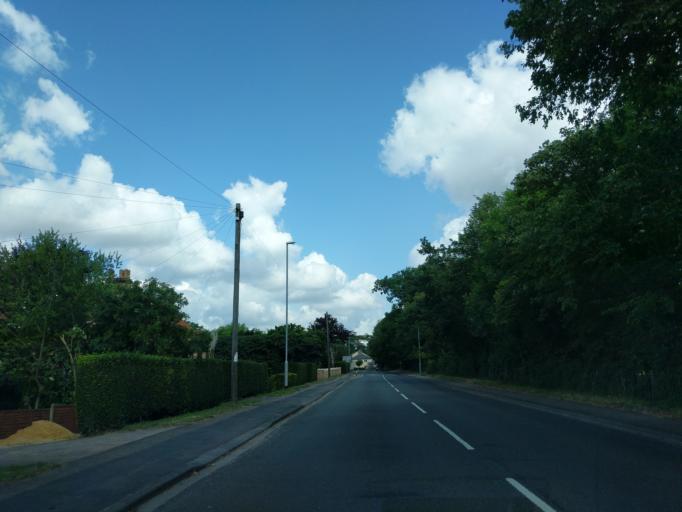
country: GB
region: England
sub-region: Suffolk
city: Exning
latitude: 52.3043
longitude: 0.3861
